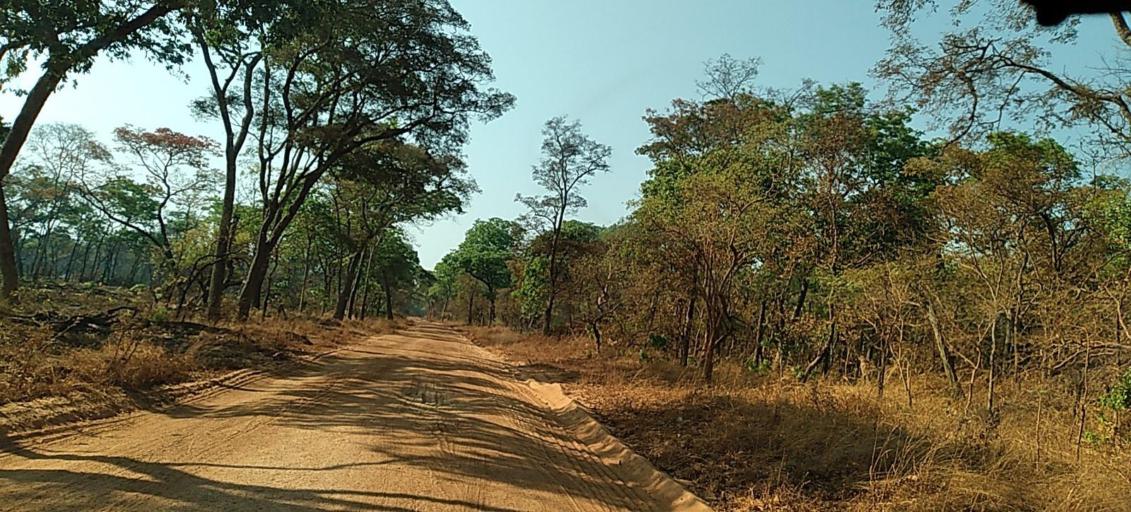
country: ZM
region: North-Western
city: Kasempa
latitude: -13.6735
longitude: 26.0182
